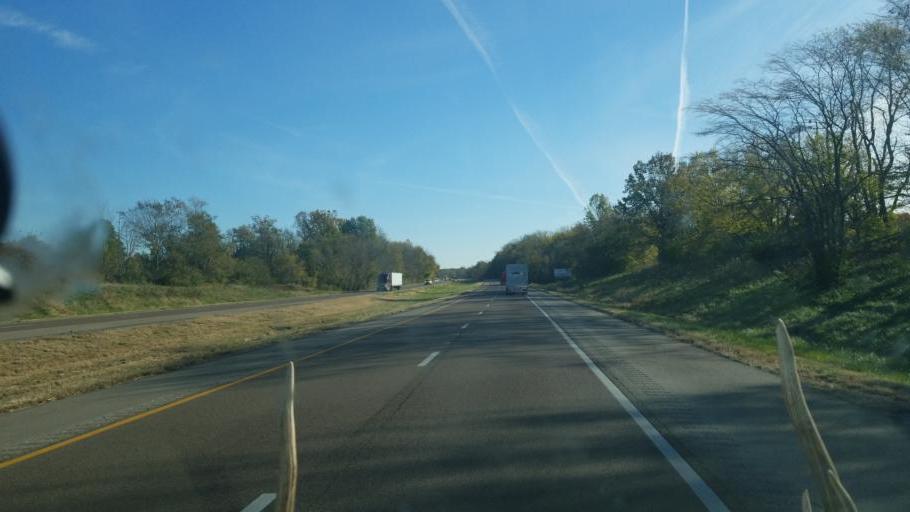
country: US
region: Illinois
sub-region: Madison County
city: Troy
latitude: 38.7567
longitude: -89.8461
